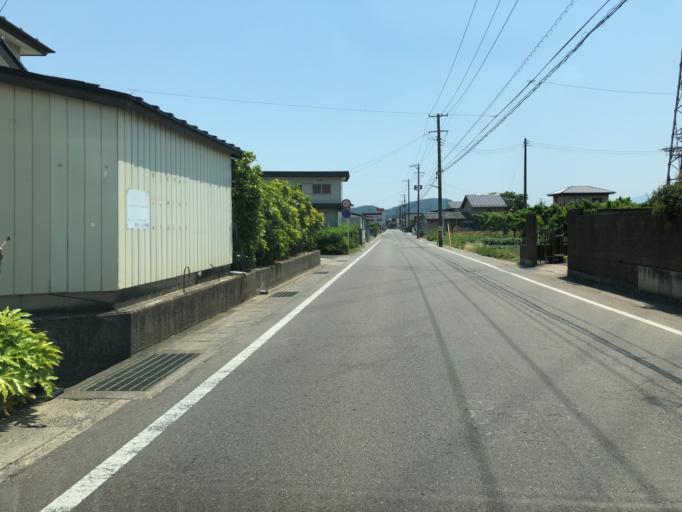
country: JP
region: Fukushima
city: Fukushima-shi
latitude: 37.8054
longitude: 140.4738
